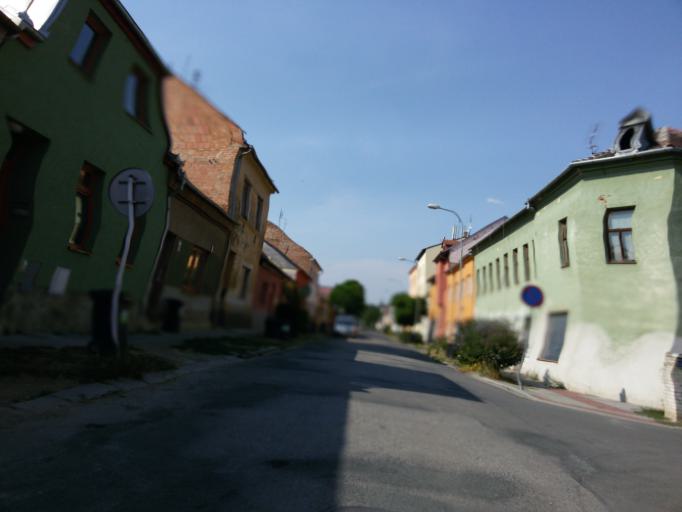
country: CZ
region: South Moravian
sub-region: Mesto Brno
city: Brno
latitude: 49.2220
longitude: 16.5999
